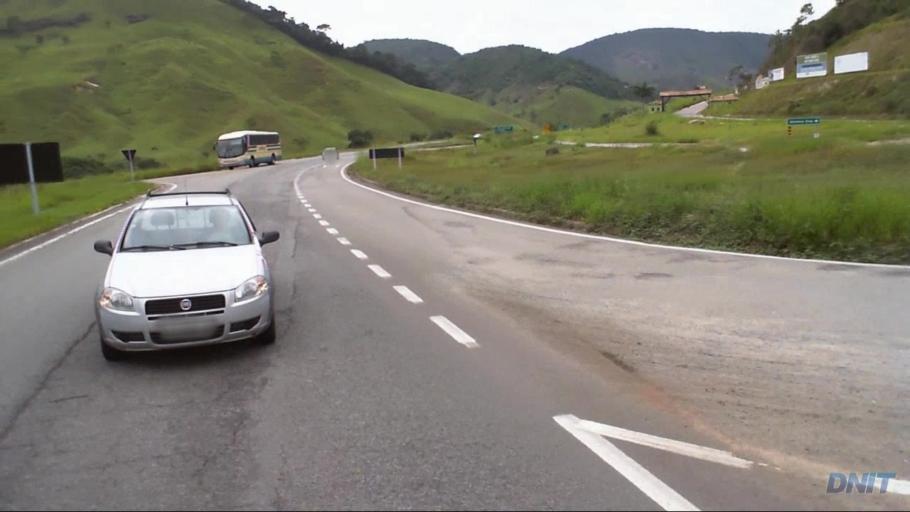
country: BR
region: Minas Gerais
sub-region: Timoteo
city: Timoteo
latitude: -19.6178
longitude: -42.8500
